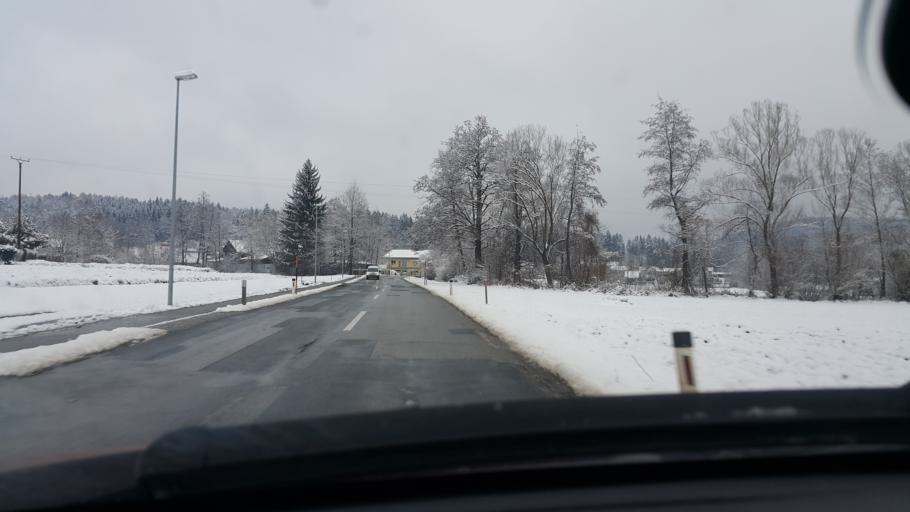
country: AT
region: Styria
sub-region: Politischer Bezirk Graz-Umgebung
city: Hitzendorf
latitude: 47.0600
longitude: 15.2925
